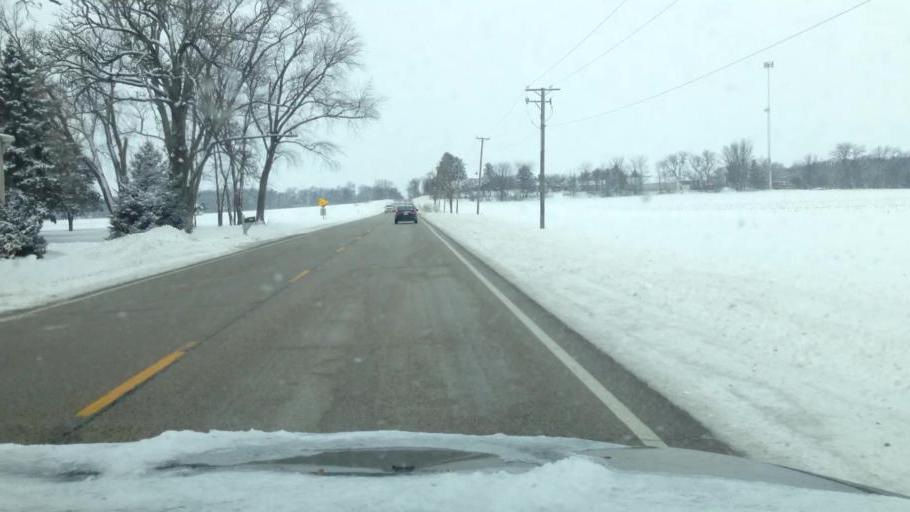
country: US
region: Illinois
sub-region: McHenry County
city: Hebron
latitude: 42.4000
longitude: -88.4382
